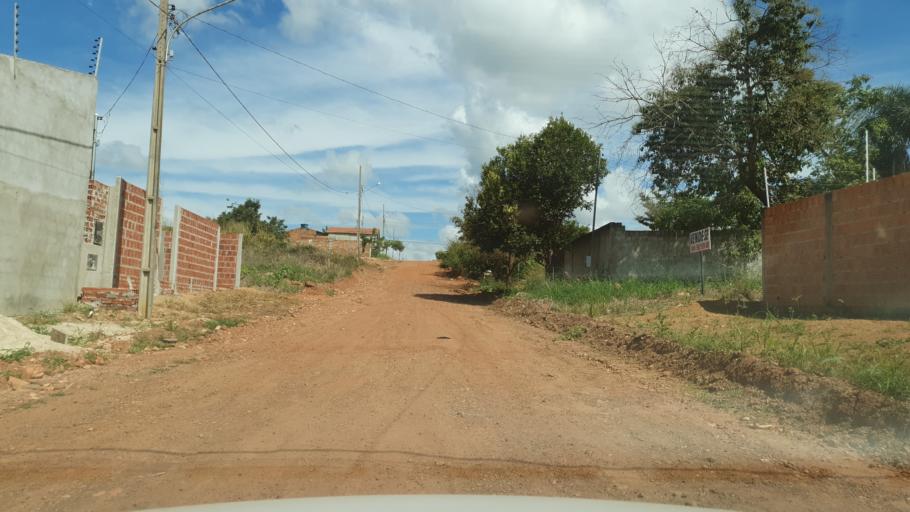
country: BR
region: Mato Grosso
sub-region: Pontes E Lacerda
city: Pontes e Lacerda
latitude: -15.2518
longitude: -59.3133
